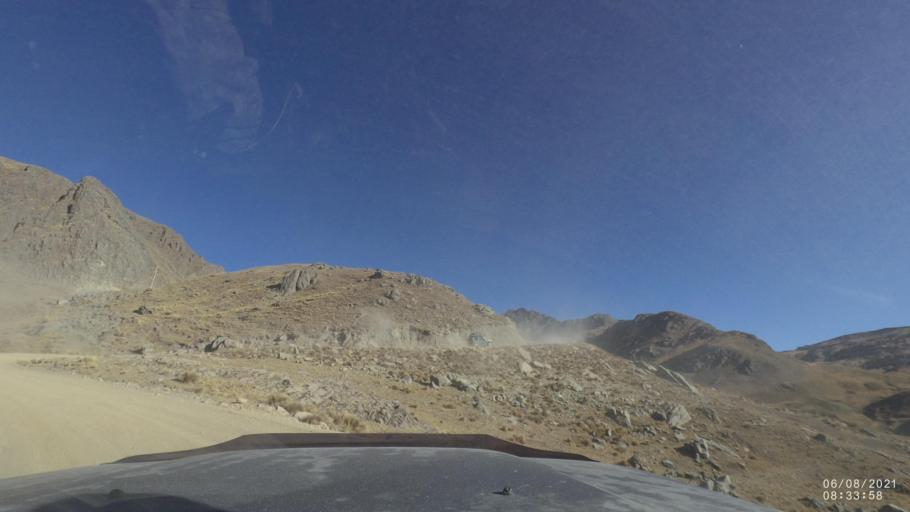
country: BO
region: Cochabamba
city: Sipe Sipe
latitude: -17.1792
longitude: -66.3783
